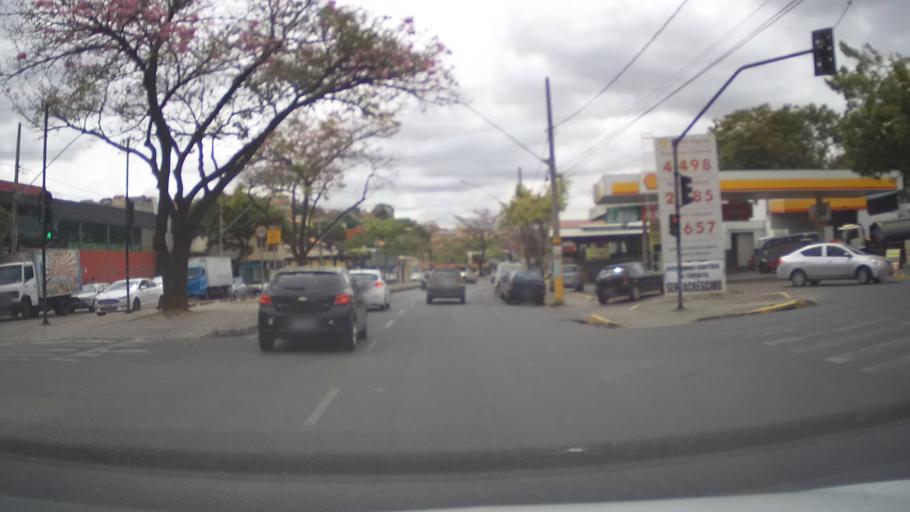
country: BR
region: Minas Gerais
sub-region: Belo Horizonte
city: Belo Horizonte
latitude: -19.8414
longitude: -43.9219
